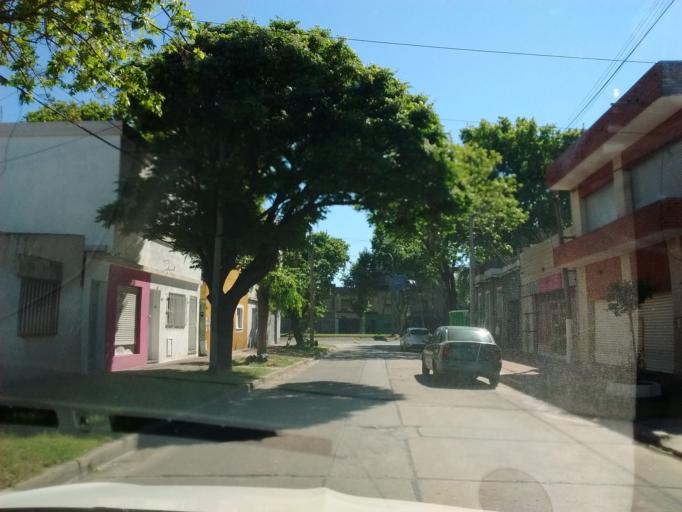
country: AR
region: Santa Fe
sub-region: Departamento de Rosario
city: Rosario
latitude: -32.9116
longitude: -60.6864
